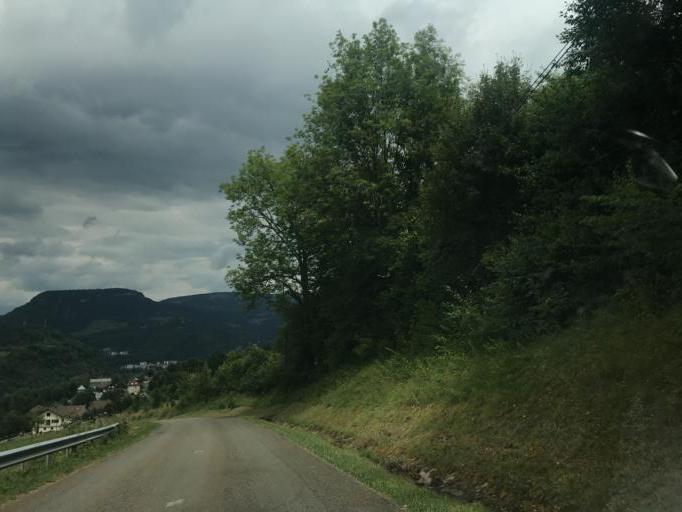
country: FR
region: Franche-Comte
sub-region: Departement du Jura
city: Saint-Claude
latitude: 46.3559
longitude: 5.8582
